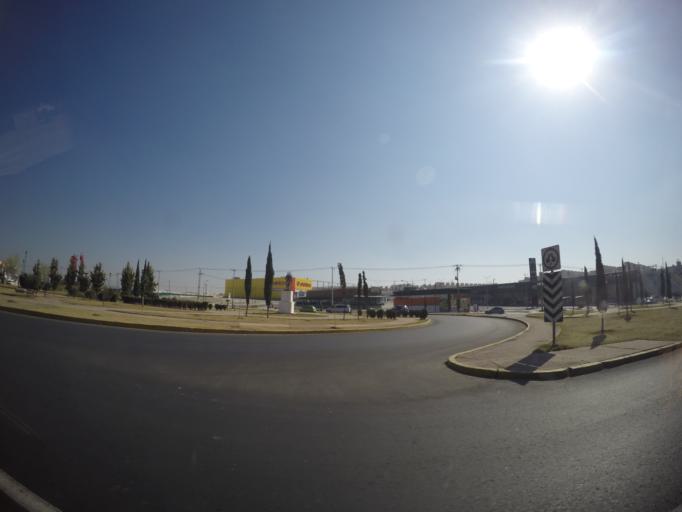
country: MX
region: Mexico
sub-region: Atenco
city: Colonia el Salado
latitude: 19.5857
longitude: -99.0222
